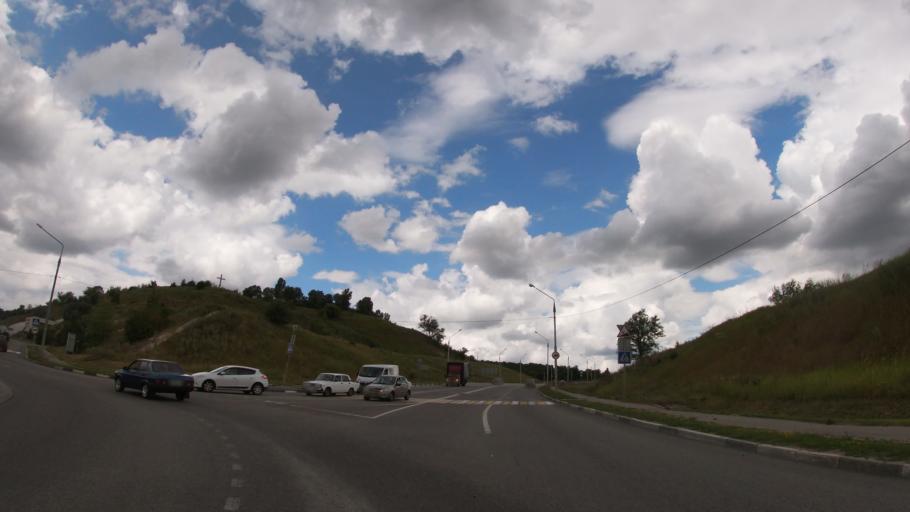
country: RU
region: Belgorod
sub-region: Belgorodskiy Rayon
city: Belgorod
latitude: 50.6175
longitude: 36.6165
